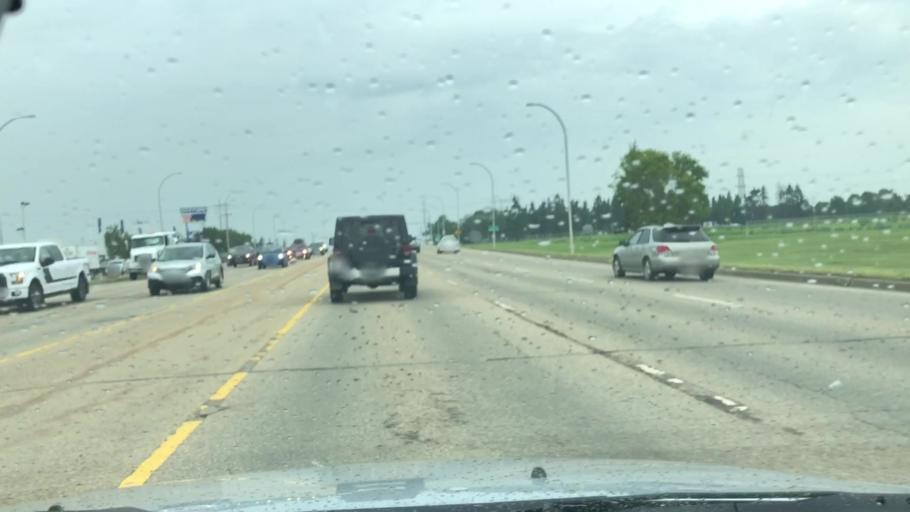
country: CA
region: Alberta
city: St. Albert
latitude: 53.6094
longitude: -113.5872
